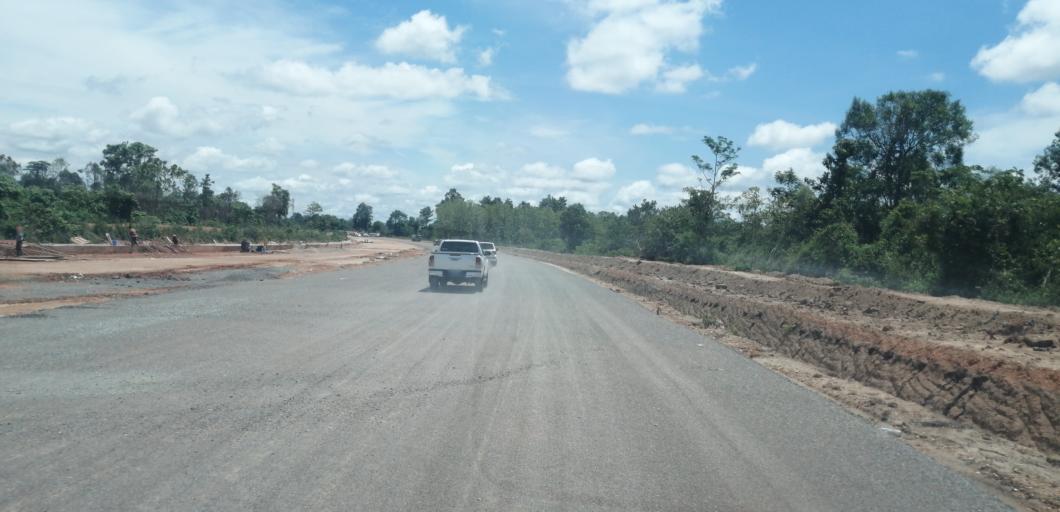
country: TH
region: Nong Khai
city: Sangkhom
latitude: 18.2277
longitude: 102.4824
